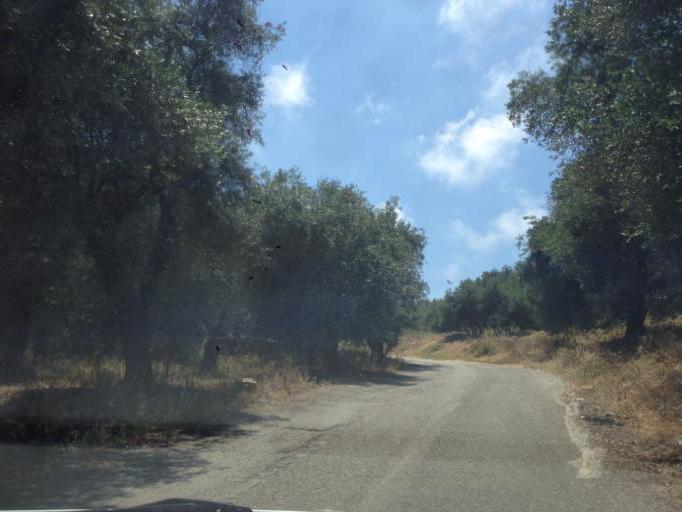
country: GR
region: Ionian Islands
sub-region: Nomos Kerkyras
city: Acharavi
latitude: 39.8027
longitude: 19.8517
